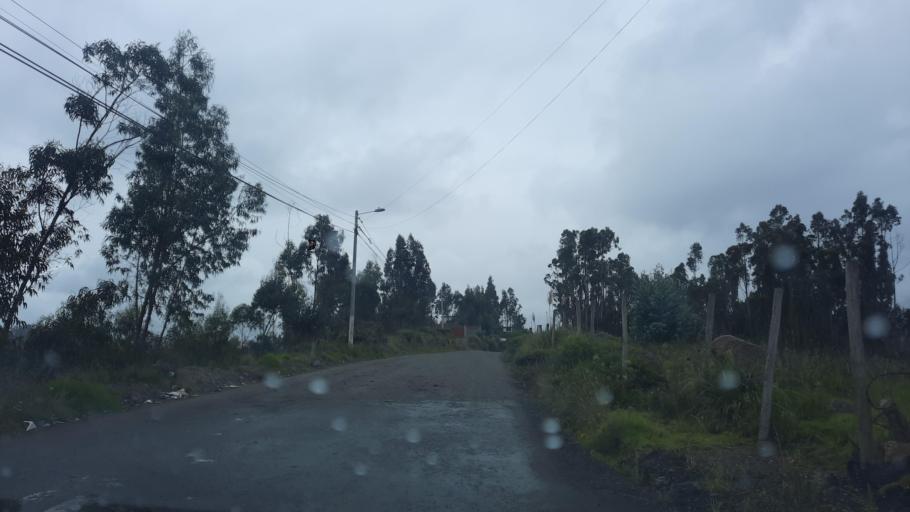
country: EC
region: Chimborazo
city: Riobamba
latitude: -1.6874
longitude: -78.6564
